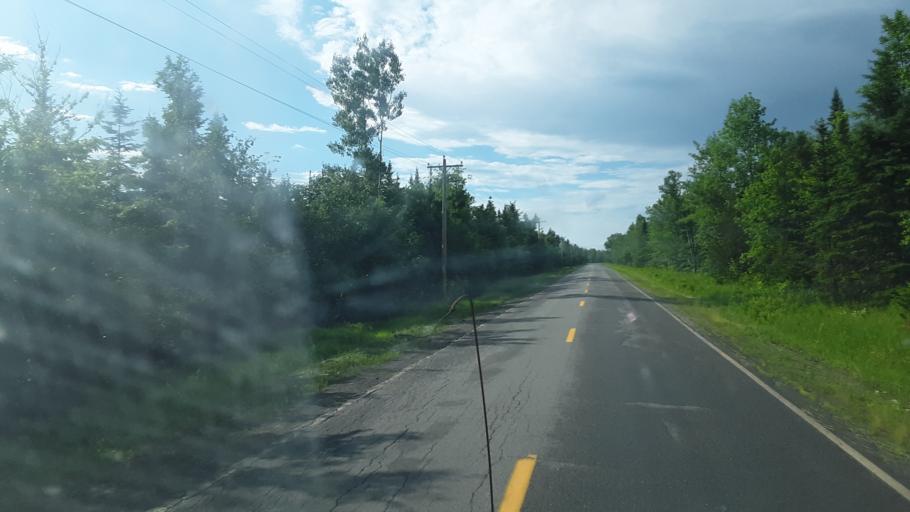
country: US
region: Maine
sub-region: Washington County
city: Calais
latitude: 45.2000
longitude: -67.5266
